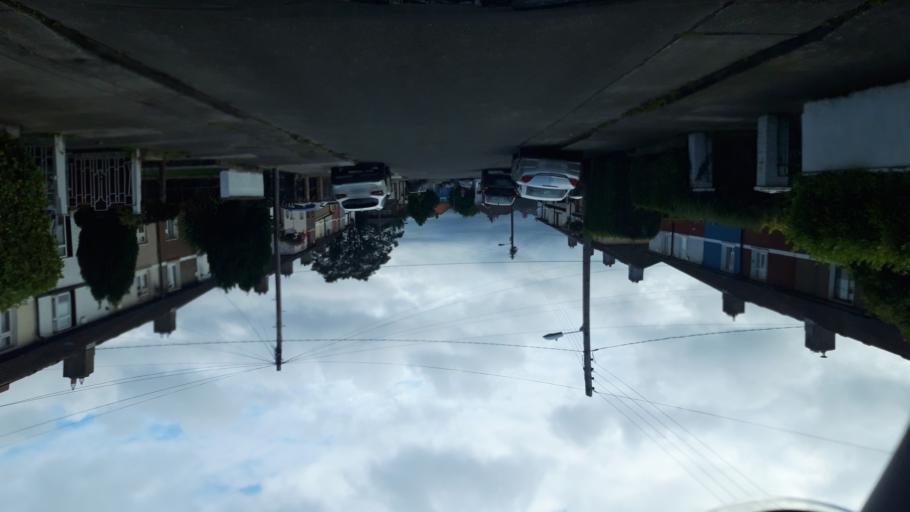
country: IE
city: Donnycarney
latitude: 53.3750
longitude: -6.2227
